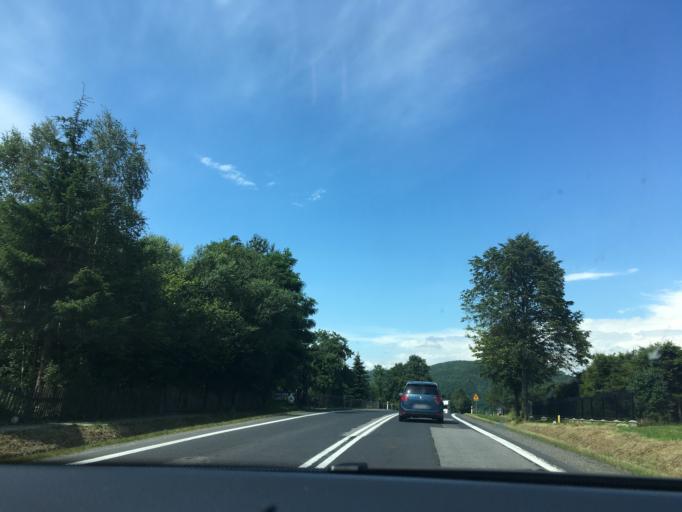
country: PL
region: Subcarpathian Voivodeship
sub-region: Powiat krosnienski
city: Dukla
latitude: 49.4539
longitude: 21.6932
